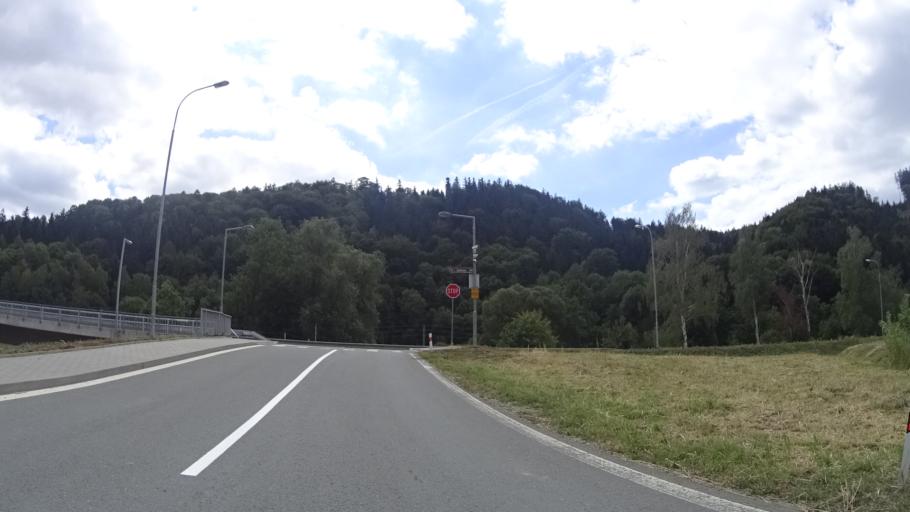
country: CZ
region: Pardubicky
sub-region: Okres Usti nad Orlici
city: Usti nad Orlici
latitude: 49.9706
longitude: 16.3805
